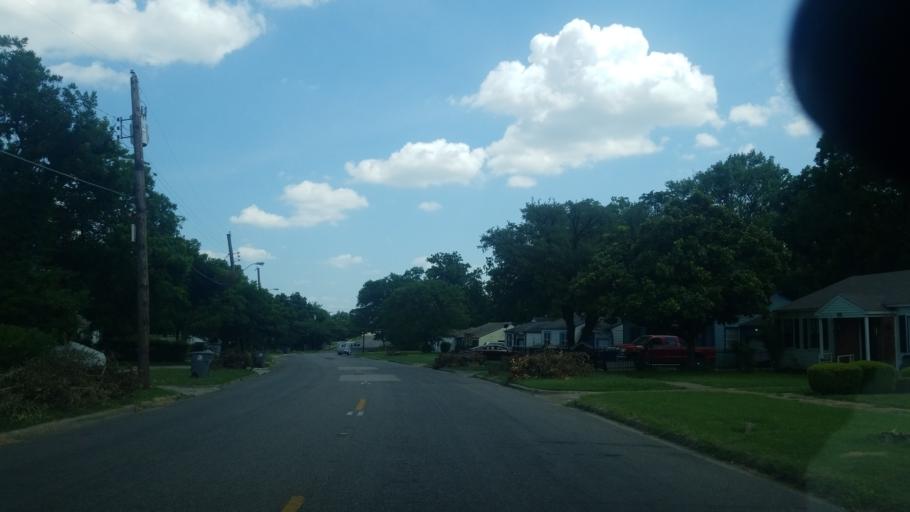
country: US
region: Texas
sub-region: Dallas County
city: Dallas
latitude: 32.7153
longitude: -96.7868
